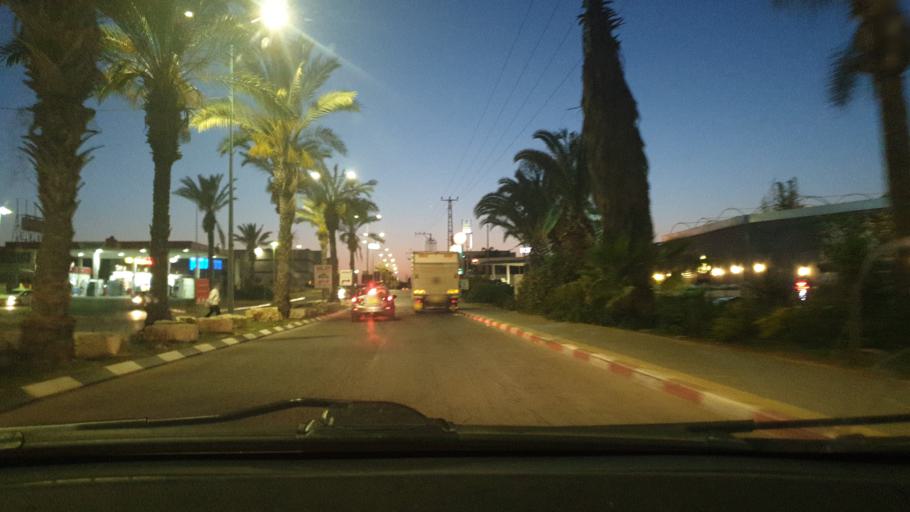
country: IL
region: Central District
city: Bene 'Ayish
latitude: 31.7996
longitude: 34.7619
